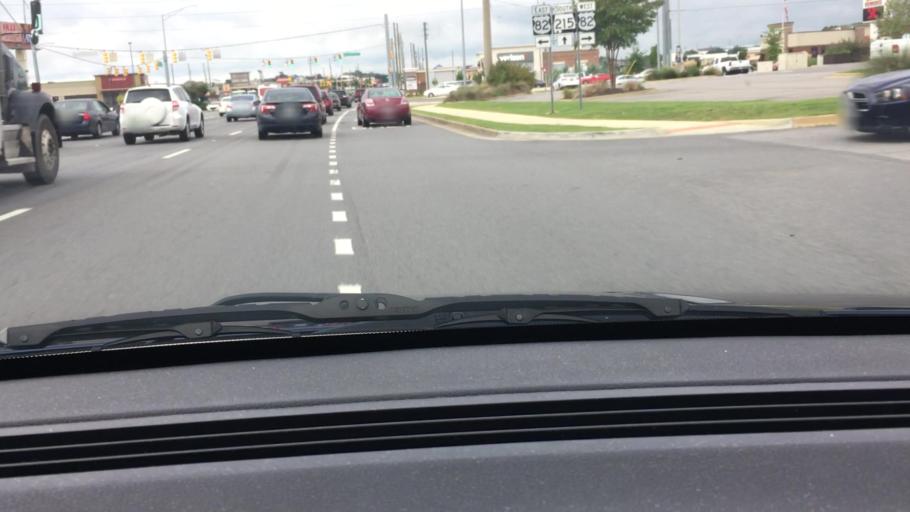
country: US
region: Alabama
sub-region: Tuscaloosa County
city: Tuscaloosa
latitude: 33.1971
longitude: -87.5246
